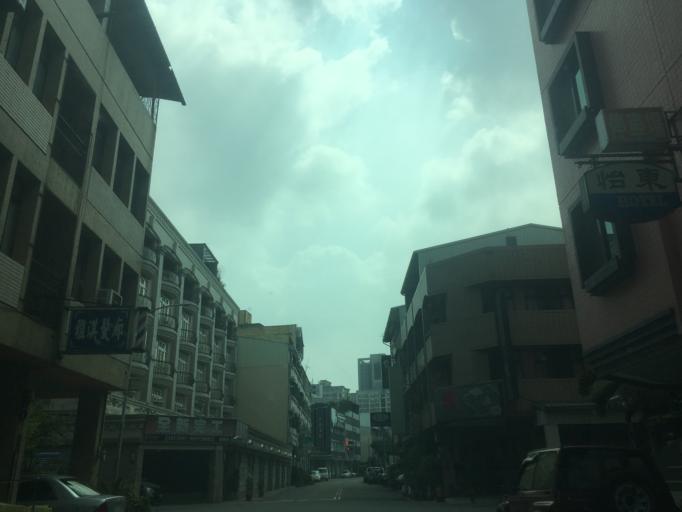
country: TW
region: Taiwan
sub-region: Taichung City
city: Taichung
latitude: 24.1723
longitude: 120.6749
